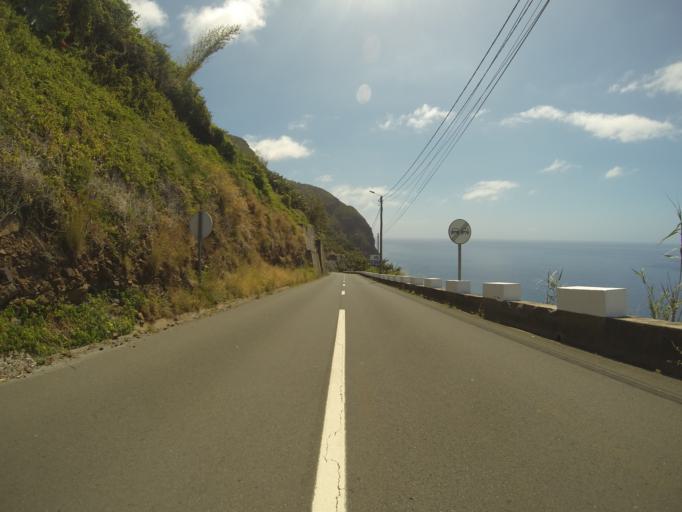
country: PT
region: Madeira
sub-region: Calheta
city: Arco da Calheta
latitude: 32.7084
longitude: -17.1478
